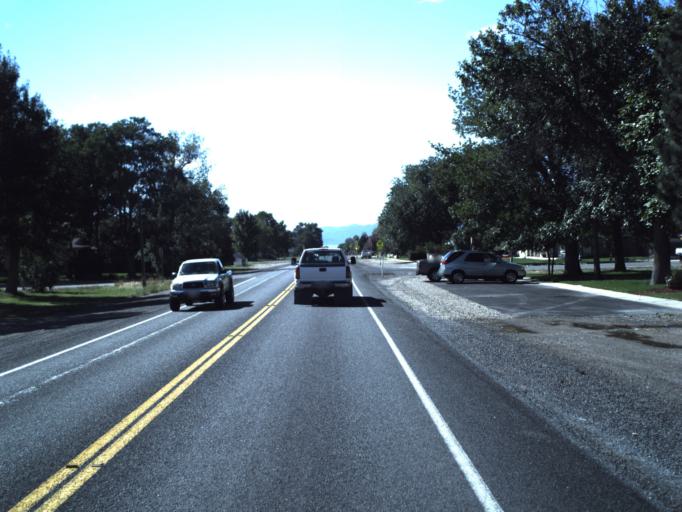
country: US
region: Utah
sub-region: Beaver County
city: Beaver
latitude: 38.2770
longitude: -112.6283
